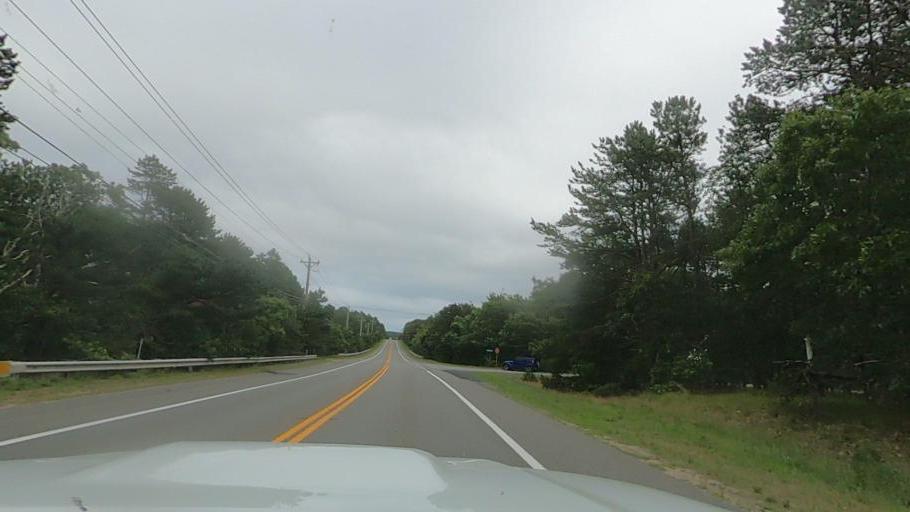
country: US
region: Massachusetts
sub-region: Barnstable County
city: Truro
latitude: 41.9787
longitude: -70.0408
